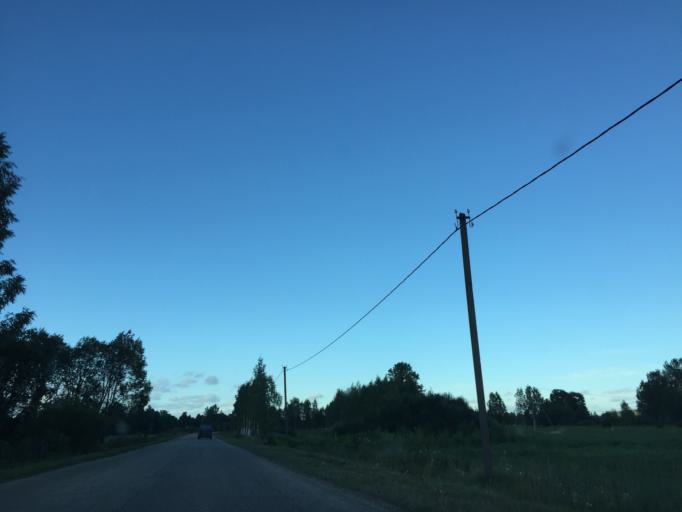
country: LV
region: Plavinu
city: Plavinas
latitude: 56.6081
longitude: 25.7986
